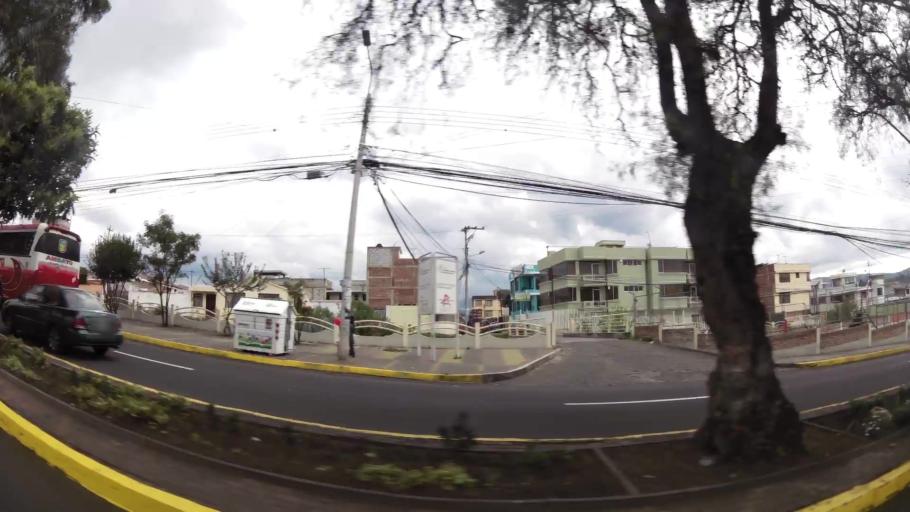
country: EC
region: Tungurahua
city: Ambato
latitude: -1.2341
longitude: -78.6137
